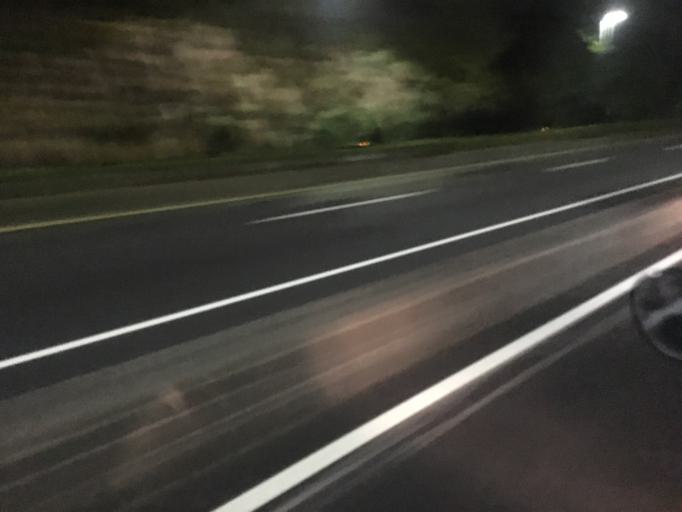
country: TW
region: Taiwan
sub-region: Hsinchu
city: Hsinchu
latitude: 24.7689
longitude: 120.9529
